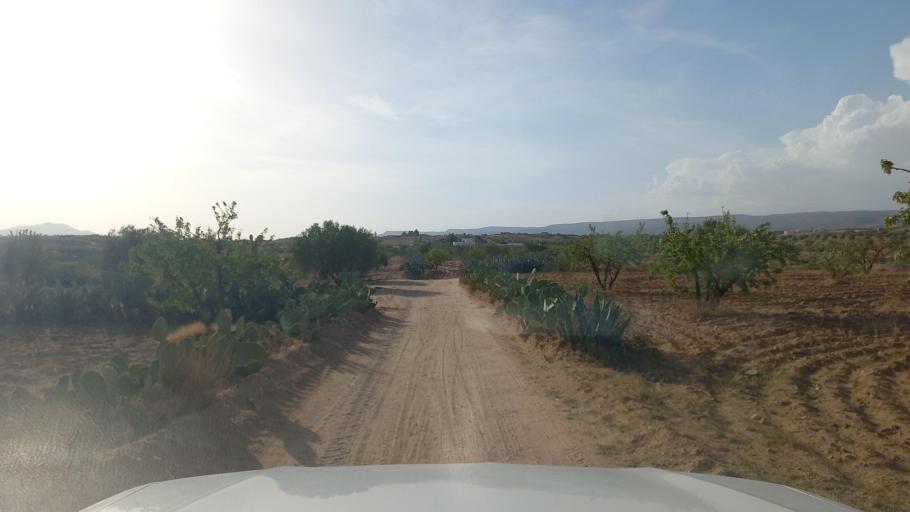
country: TN
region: Al Qasrayn
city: Kasserine
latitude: 35.2369
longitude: 8.9139
